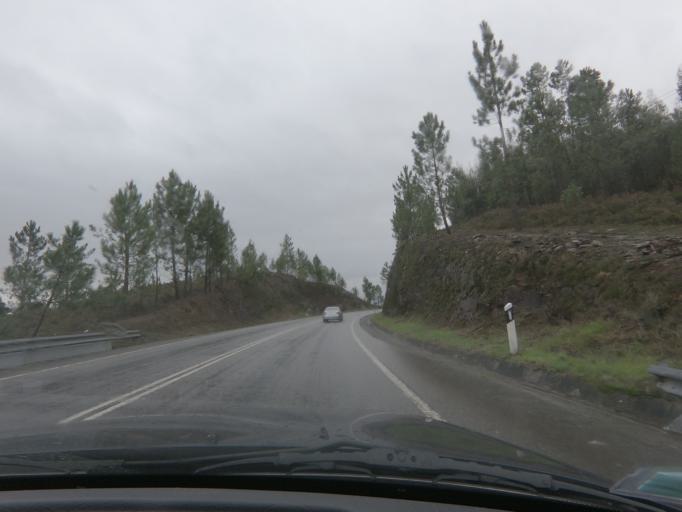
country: PT
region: Porto
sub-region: Amarante
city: Amarante
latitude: 41.3270
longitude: -8.0413
